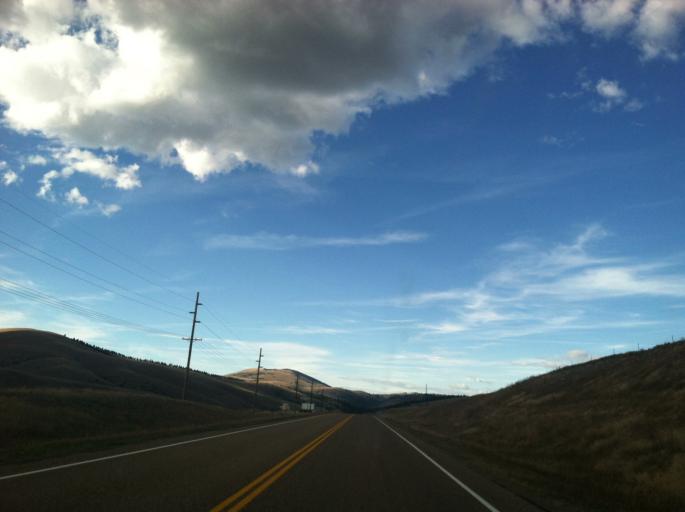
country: US
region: Montana
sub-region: Granite County
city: Philipsburg
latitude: 46.3659
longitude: -113.3142
